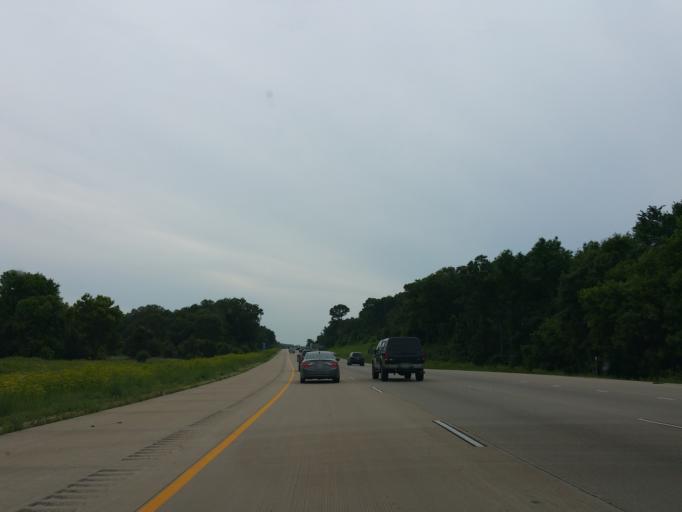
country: US
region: Wisconsin
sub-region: Columbia County
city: Poynette
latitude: 43.3871
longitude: -89.4664
